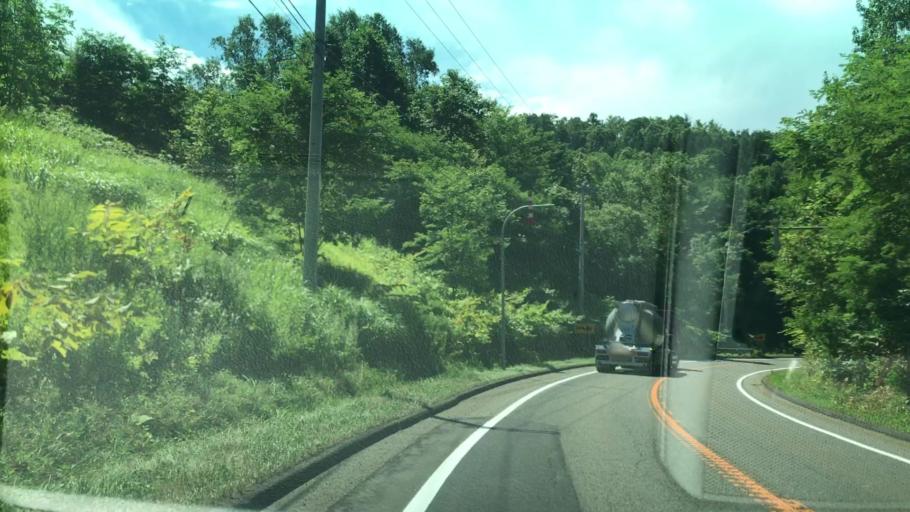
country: JP
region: Hokkaido
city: Shimo-furano
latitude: 42.9018
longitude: 142.4385
